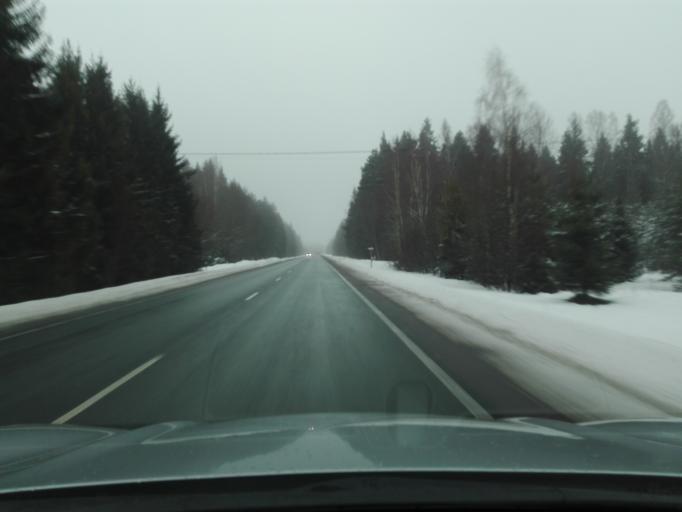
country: EE
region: Raplamaa
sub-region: Kohila vald
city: Kohila
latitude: 59.1497
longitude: 24.7826
